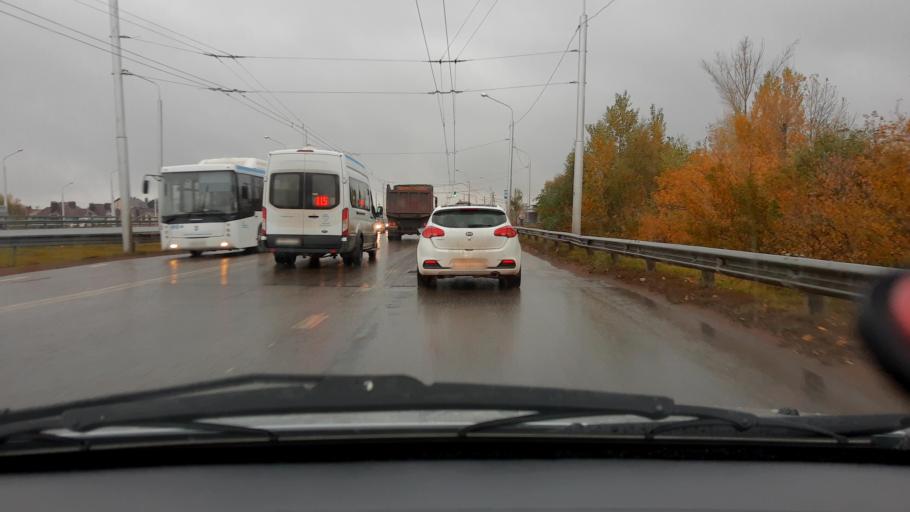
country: RU
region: Bashkortostan
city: Ufa
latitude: 54.7668
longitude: 55.9559
